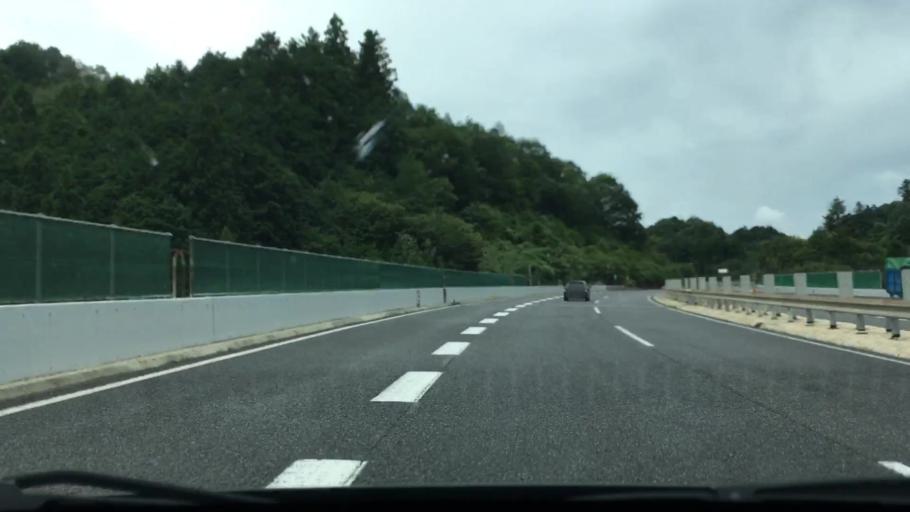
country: JP
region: Hiroshima
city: Hiroshima-shi
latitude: 34.5166
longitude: 132.4257
